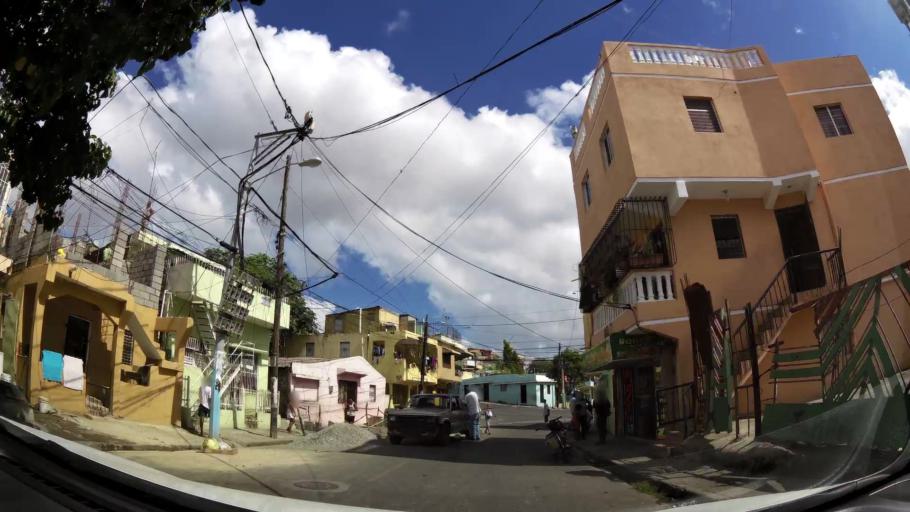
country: DO
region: Nacional
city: San Carlos
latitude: 18.4900
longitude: -69.8858
